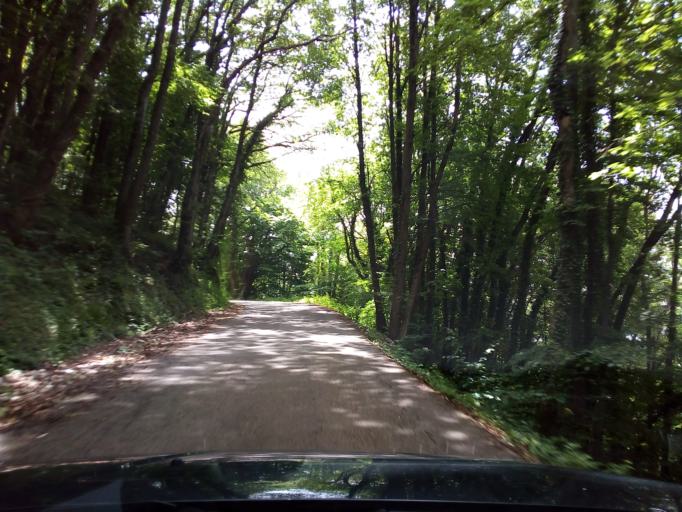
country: FR
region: Rhone-Alpes
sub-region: Departement de l'Isere
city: Herbeys
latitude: 45.1505
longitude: 5.7820
